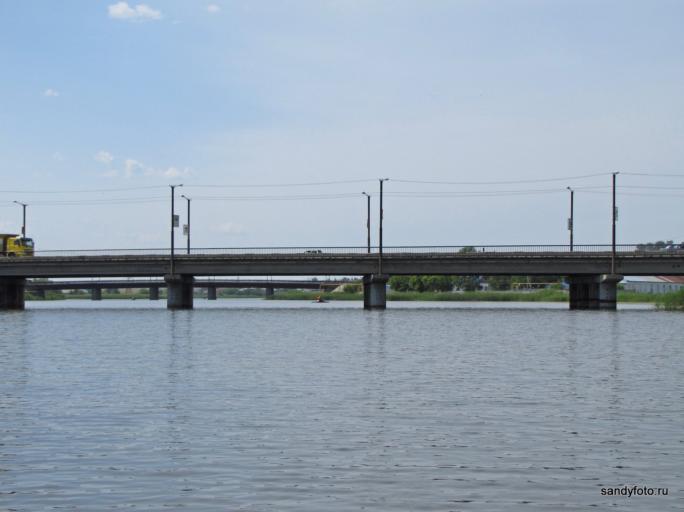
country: RU
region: Chelyabinsk
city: Troitsk
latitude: 54.0902
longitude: 61.5772
